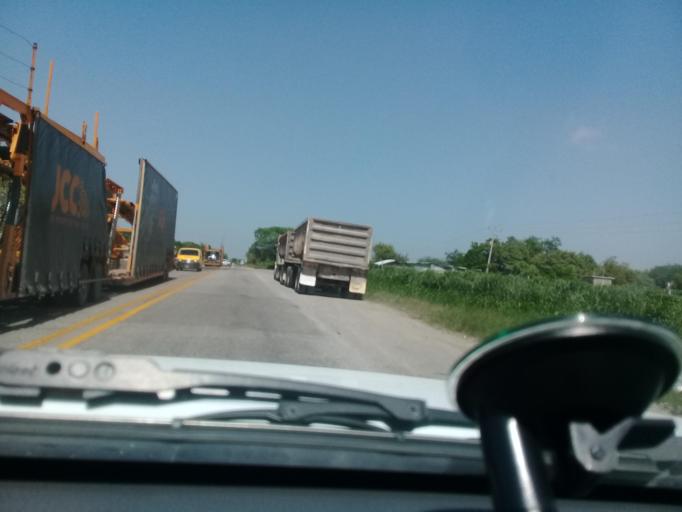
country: MX
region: Veracruz
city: Moralillo
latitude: 22.1715
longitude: -98.0487
